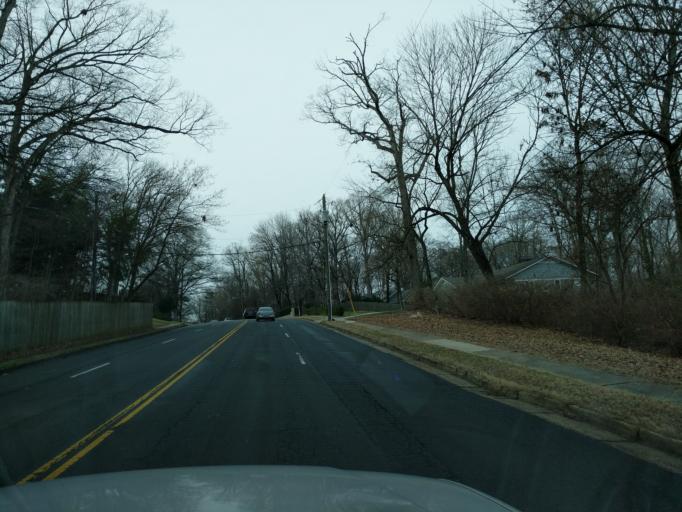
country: US
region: North Carolina
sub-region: Mecklenburg County
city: Charlotte
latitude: 35.1674
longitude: -80.8268
